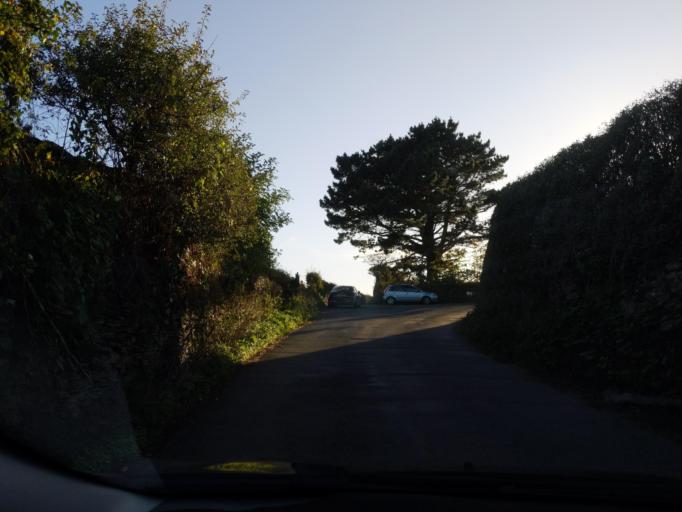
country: GB
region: England
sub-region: Plymouth
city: Plymstock
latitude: 50.3435
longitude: -4.0937
